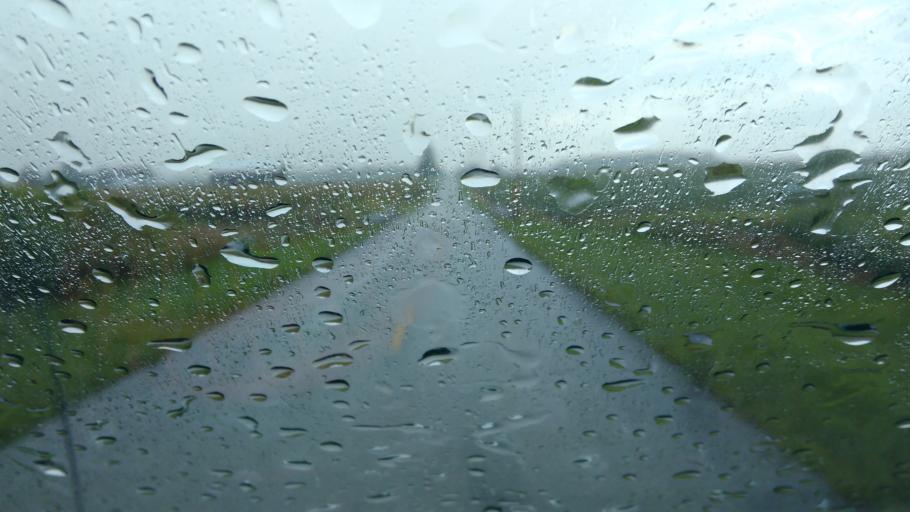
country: US
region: Ohio
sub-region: Hardin County
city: Kenton
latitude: 40.7174
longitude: -83.5874
